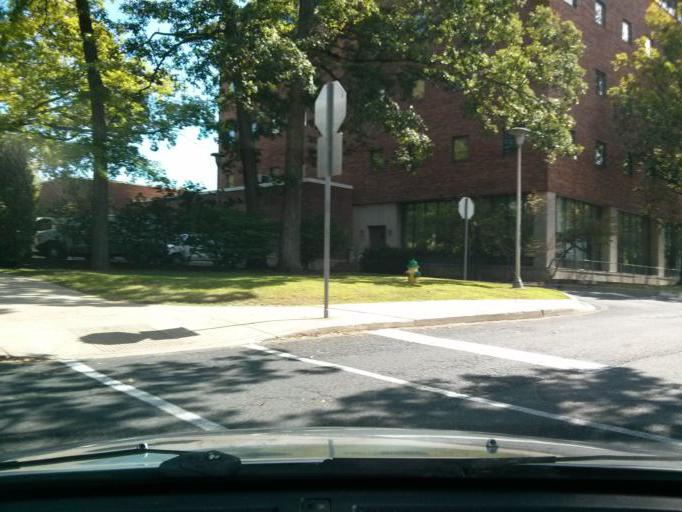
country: US
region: Pennsylvania
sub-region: Centre County
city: State College
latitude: 40.7979
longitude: -77.8714
